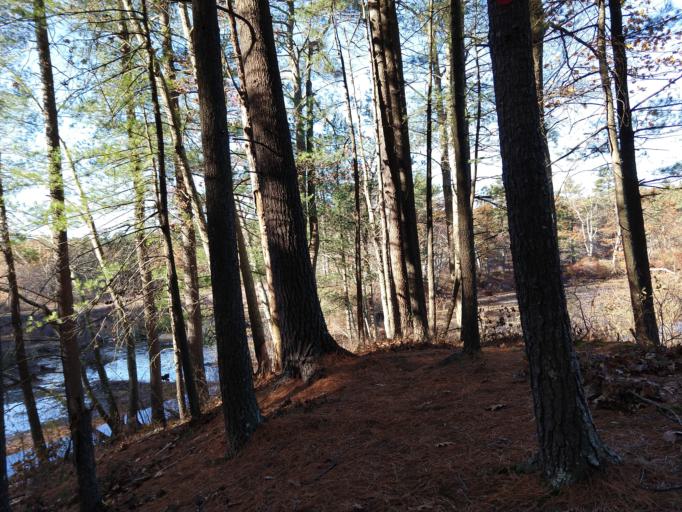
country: US
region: Massachusetts
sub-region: Middlesex County
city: Concord
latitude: 42.4874
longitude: -71.3222
